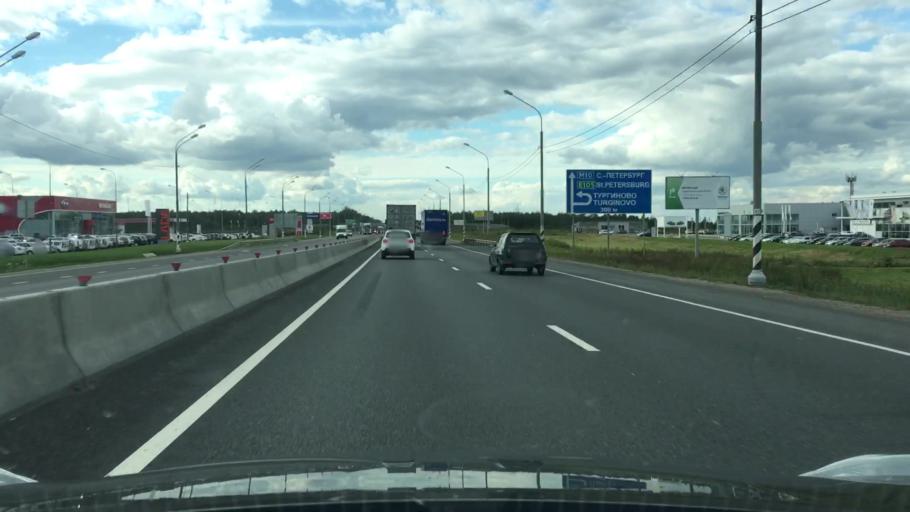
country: RU
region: Tverskaya
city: Tver
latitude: 56.7895
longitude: 35.9099
